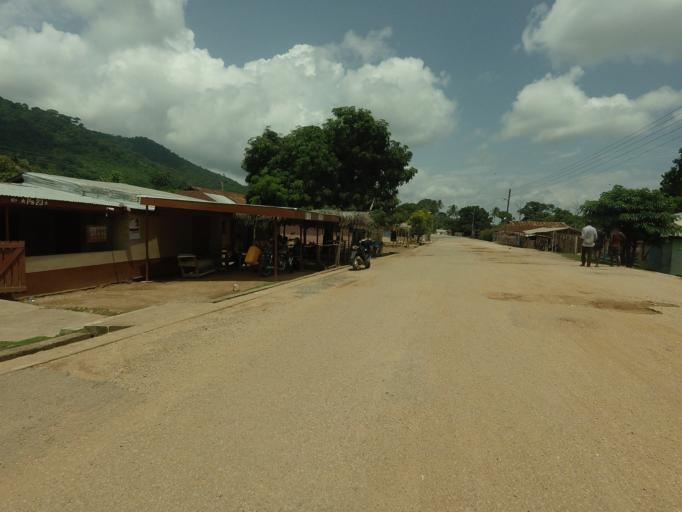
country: GH
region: Volta
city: Ho
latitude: 6.7246
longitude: 0.3424
